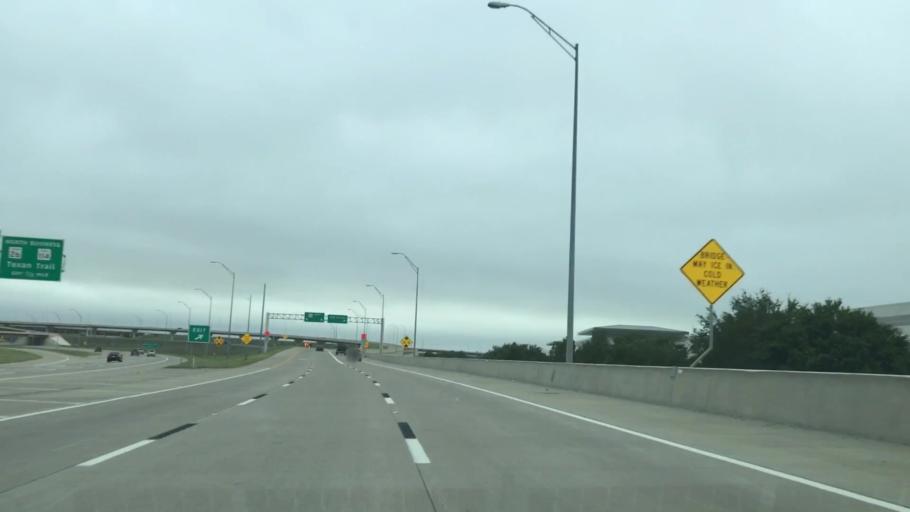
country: US
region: Texas
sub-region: Dallas County
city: Coppell
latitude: 32.9309
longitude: -97.0328
